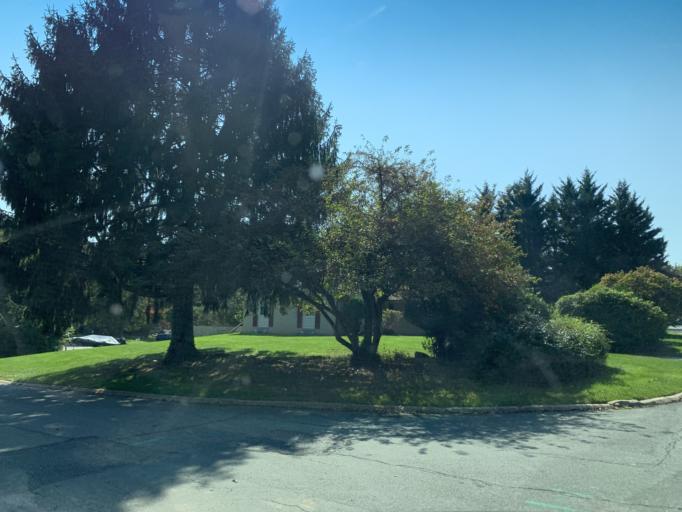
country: US
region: Maryland
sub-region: Harford County
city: South Bel Air
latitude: 39.5248
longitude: -76.3312
